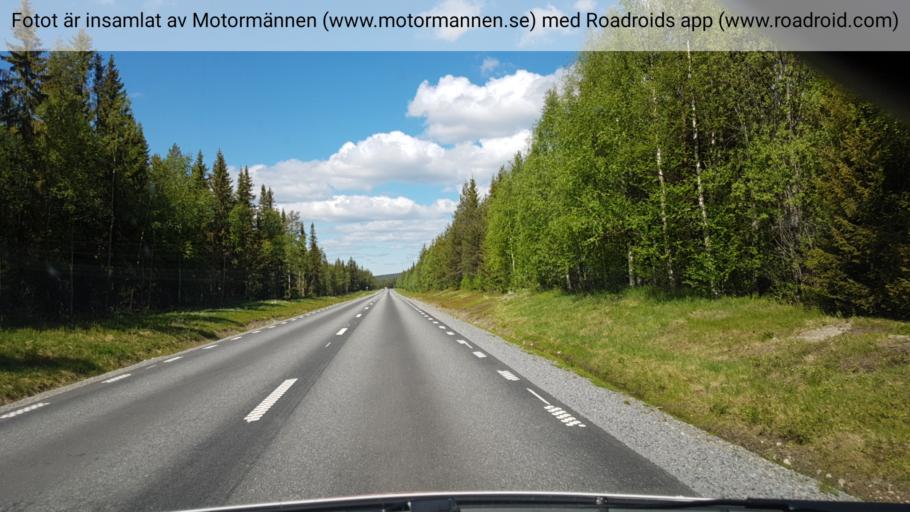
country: SE
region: Vaesterbotten
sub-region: Vilhelmina Kommun
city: Vilhelmina
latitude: 64.6928
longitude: 16.7204
